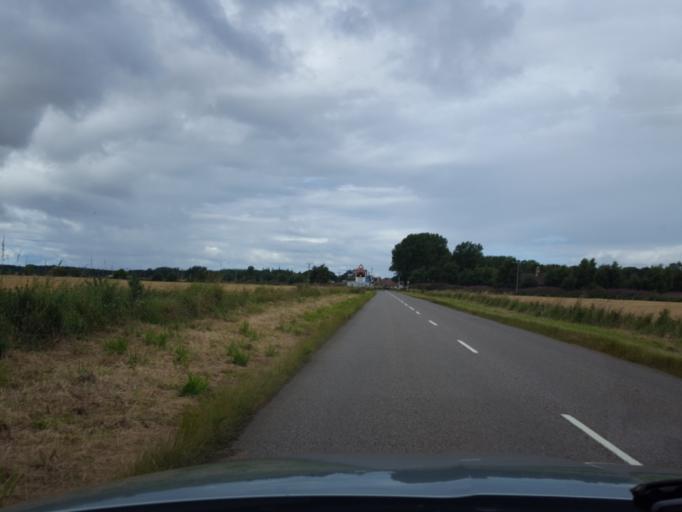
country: GB
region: Scotland
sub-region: Moray
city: Kinloss
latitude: 57.6306
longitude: -3.5550
